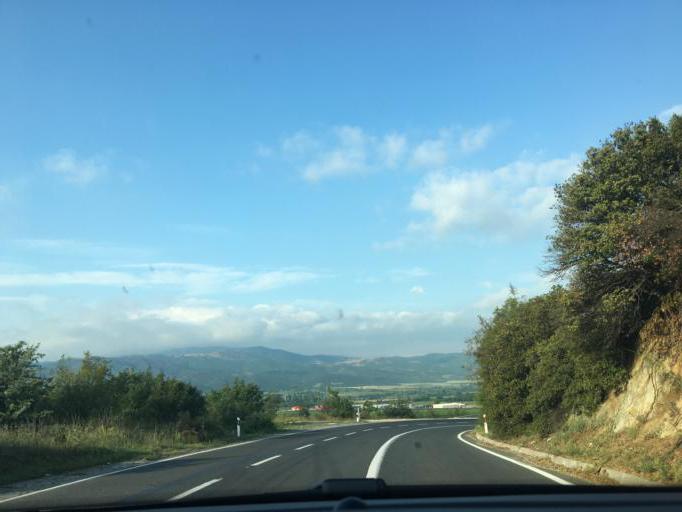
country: MK
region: Valandovo
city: Valandovo
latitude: 41.3188
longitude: 22.5963
